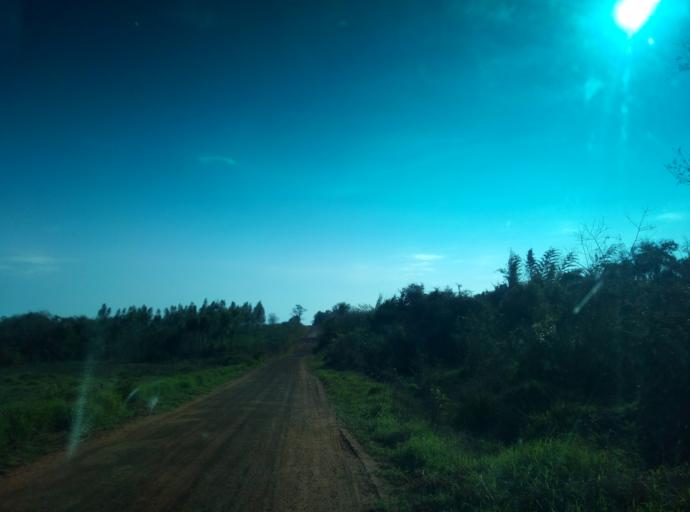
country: PY
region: Caaguazu
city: Doctor Cecilio Baez
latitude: -25.1648
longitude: -56.2253
